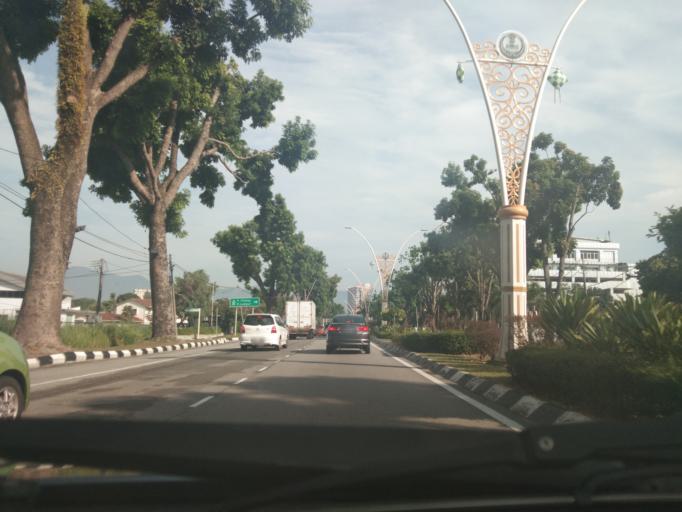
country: MY
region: Perak
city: Ipoh
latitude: 4.5897
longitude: 101.0937
